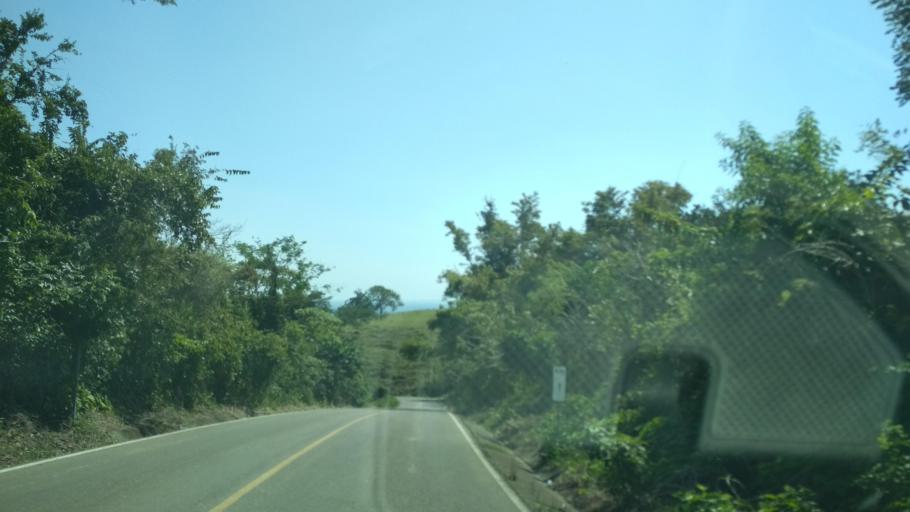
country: MX
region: Veracruz
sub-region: Papantla
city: Polutla
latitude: 20.4676
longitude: -97.2231
